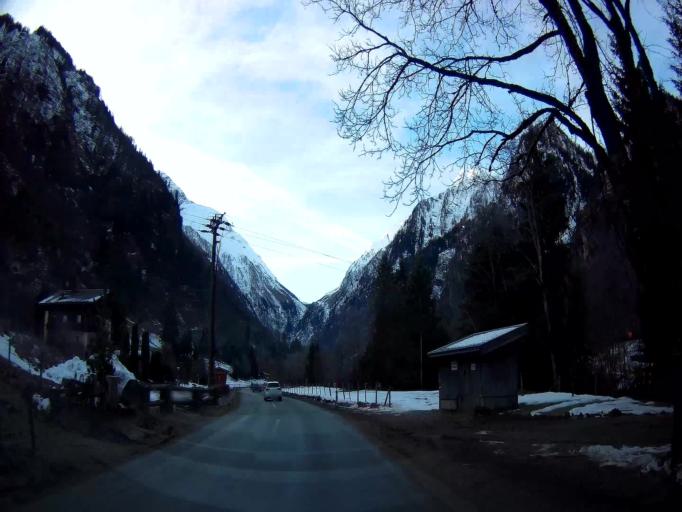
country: AT
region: Salzburg
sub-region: Politischer Bezirk Zell am See
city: Kaprun
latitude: 47.2392
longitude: 12.7309
